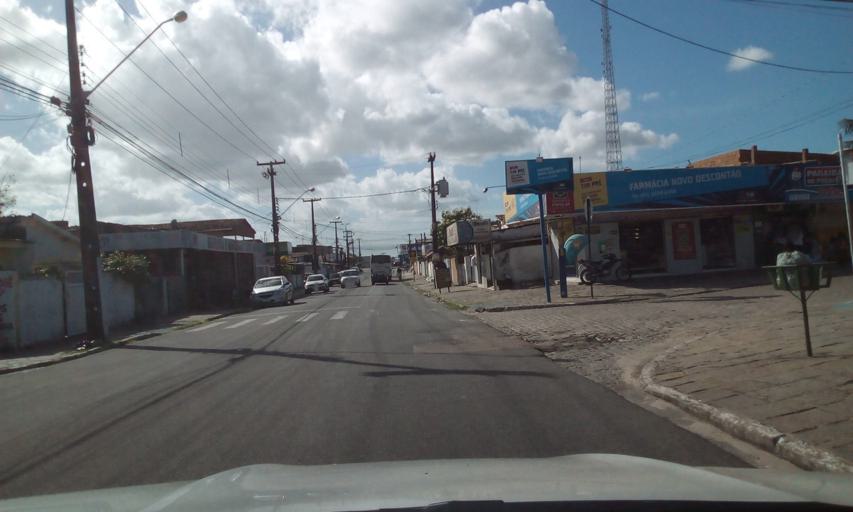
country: BR
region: Paraiba
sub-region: Joao Pessoa
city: Joao Pessoa
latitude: -7.1090
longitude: -34.8589
